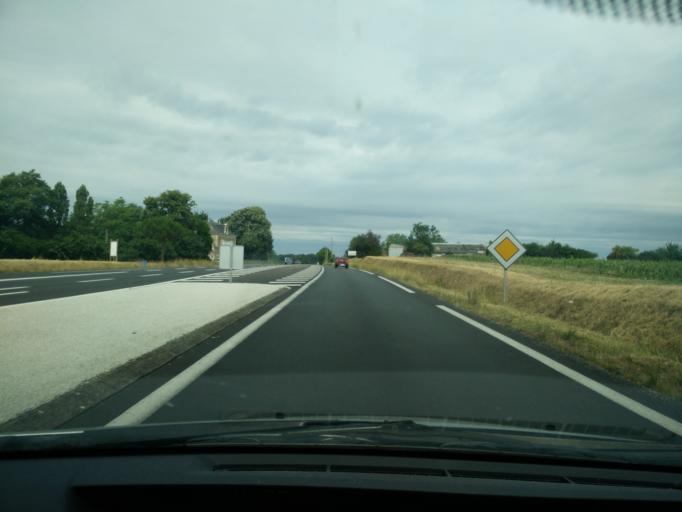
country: FR
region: Pays de la Loire
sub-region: Departement de Maine-et-Loire
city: Brissac-Quince
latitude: 47.3642
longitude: -0.4506
